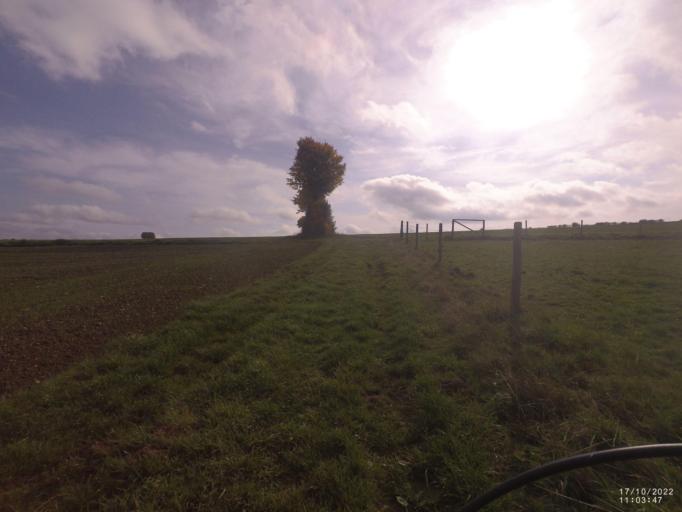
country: DE
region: Rheinland-Pfalz
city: Steiningen
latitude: 50.1847
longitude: 6.9240
